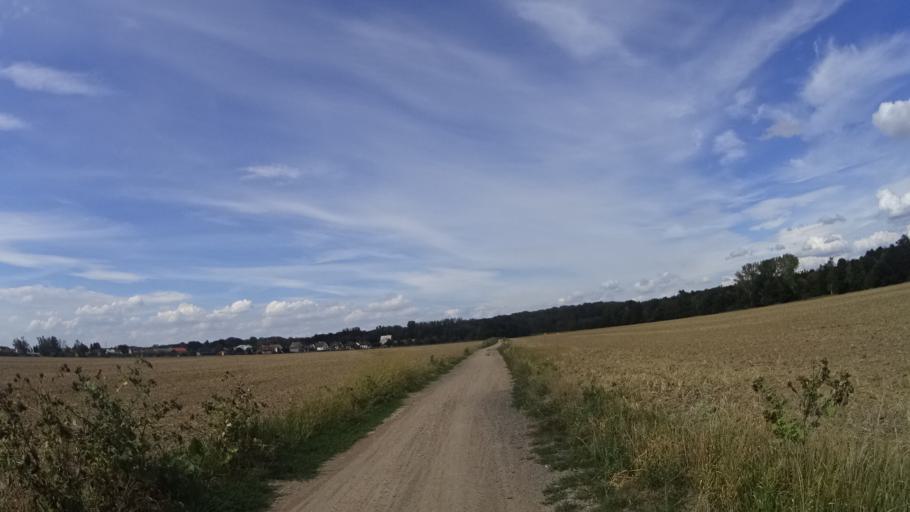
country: CZ
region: Olomoucky
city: Skrben
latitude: 49.6642
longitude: 17.1783
